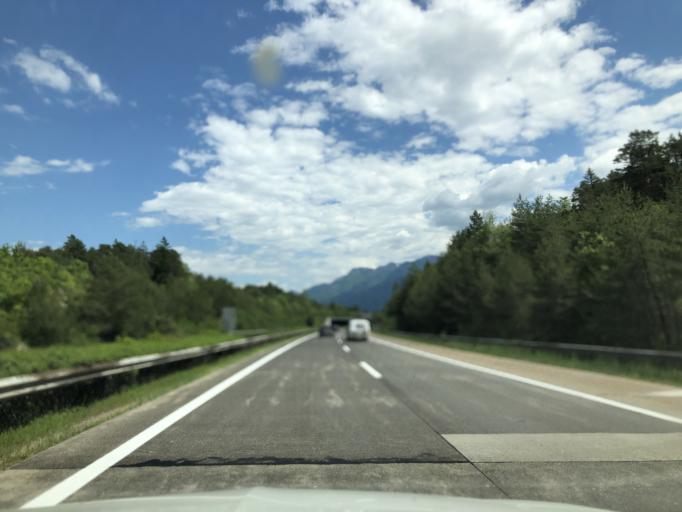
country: AT
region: Carinthia
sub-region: Politischer Bezirk Villach Land
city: Arnoldstein
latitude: 46.5674
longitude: 13.7305
